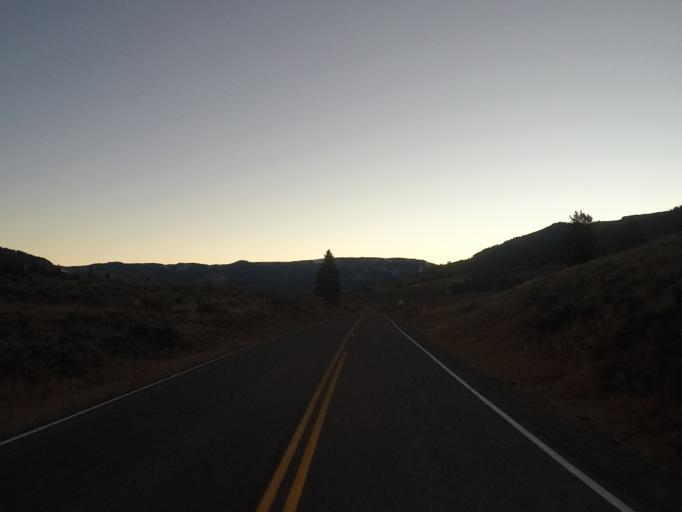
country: US
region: Montana
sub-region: Park County
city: Livingston
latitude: 44.8959
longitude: -110.1268
